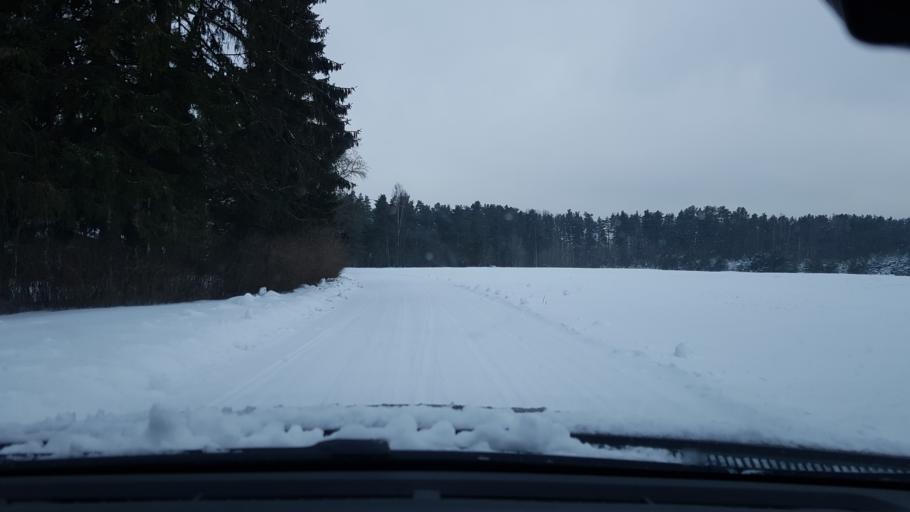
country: EE
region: Harju
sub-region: Kuusalu vald
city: Kuusalu
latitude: 59.4618
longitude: 25.4813
